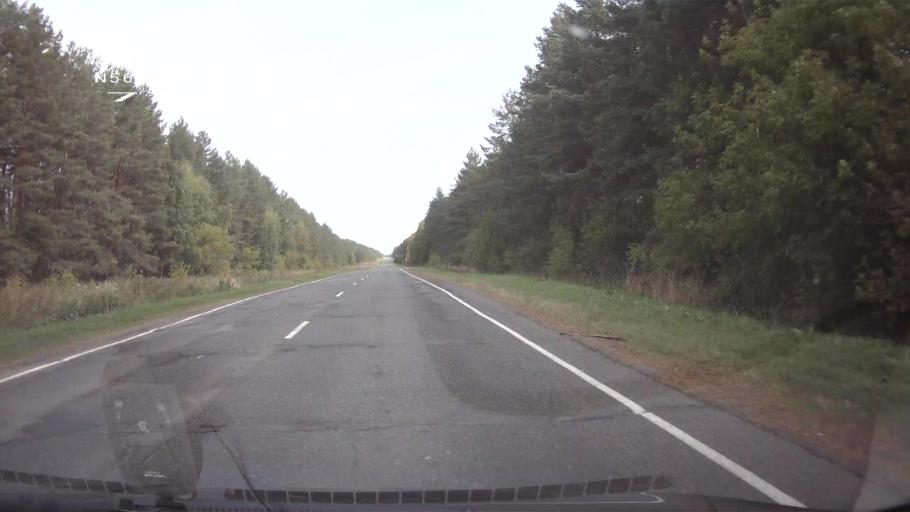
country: RU
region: Mariy-El
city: Kuzhener
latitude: 56.8214
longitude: 48.7184
